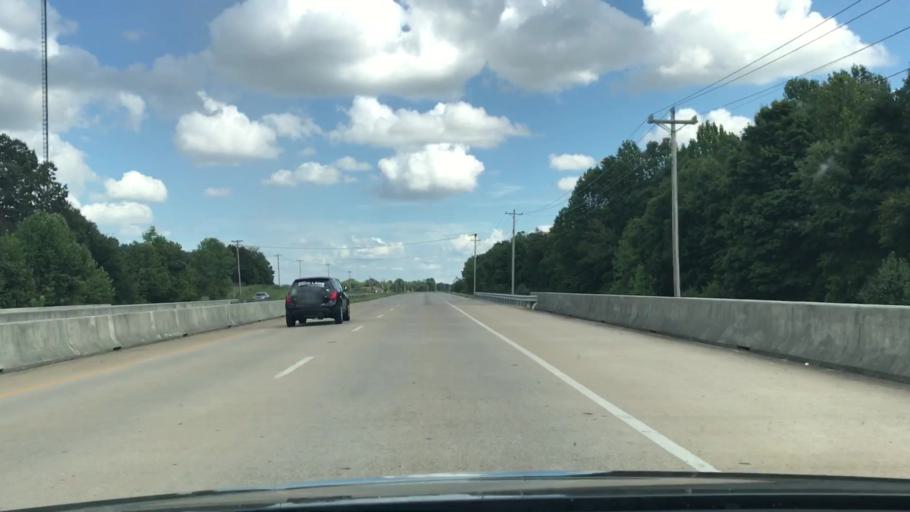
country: US
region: Kentucky
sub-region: Christian County
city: Hopkinsville
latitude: 36.8324
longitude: -87.5254
